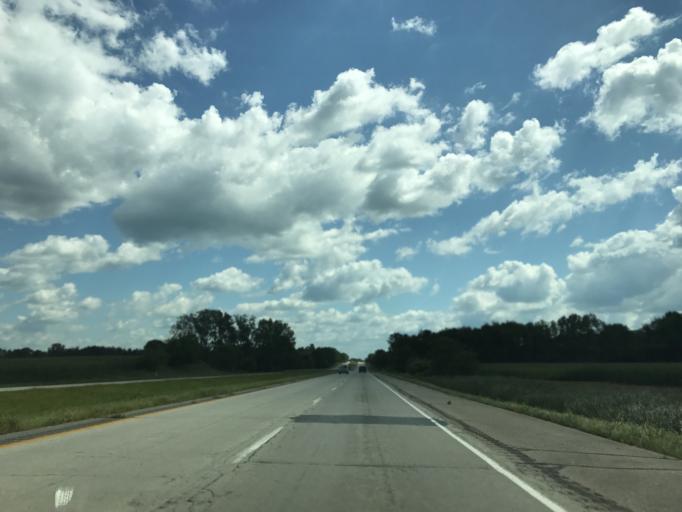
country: US
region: Indiana
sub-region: Starke County
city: Koontz Lake
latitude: 41.3645
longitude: -86.4091
